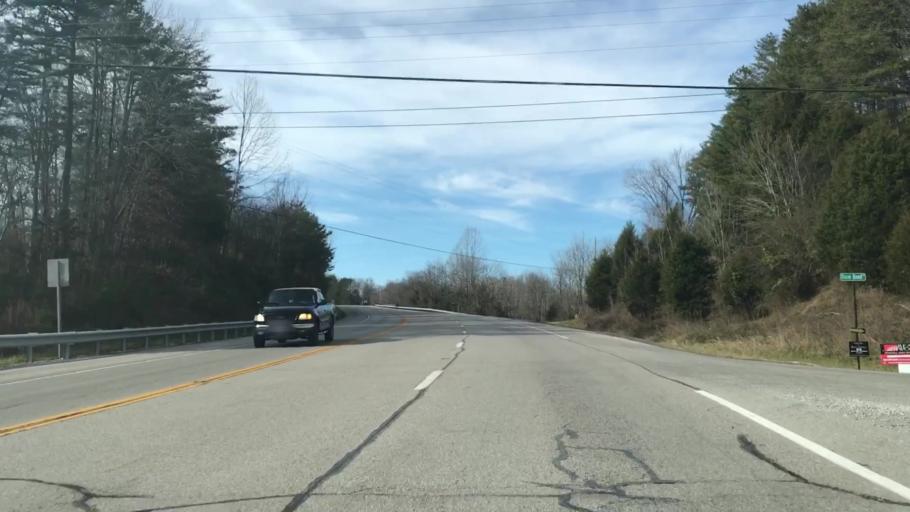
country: US
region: Kentucky
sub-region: Pulaski County
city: Somerset
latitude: 36.9451
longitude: -84.5563
